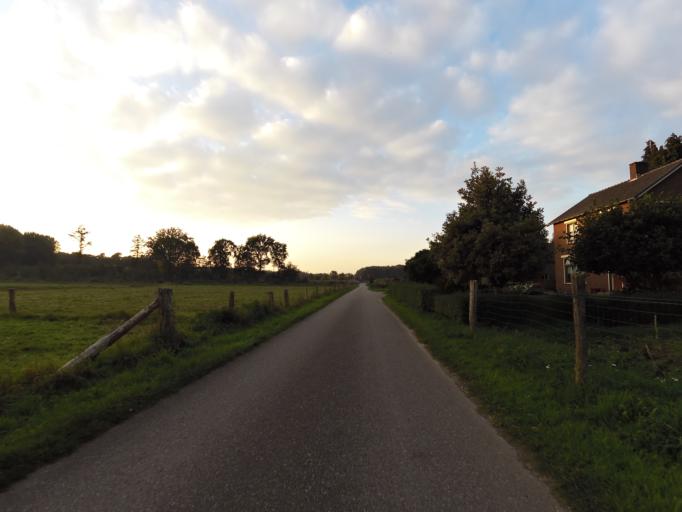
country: NL
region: Gelderland
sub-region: Gemeente Doesburg
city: Doesburg
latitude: 51.9518
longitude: 6.2012
